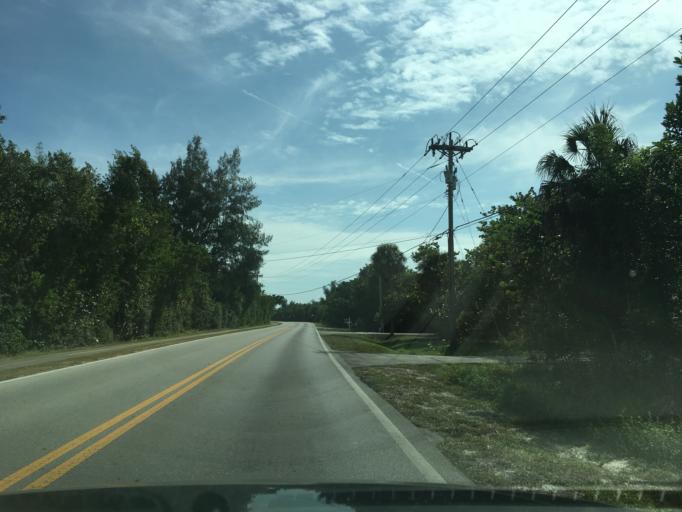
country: US
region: Florida
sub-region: Lee County
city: Saint James City
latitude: 26.4771
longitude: -82.1756
